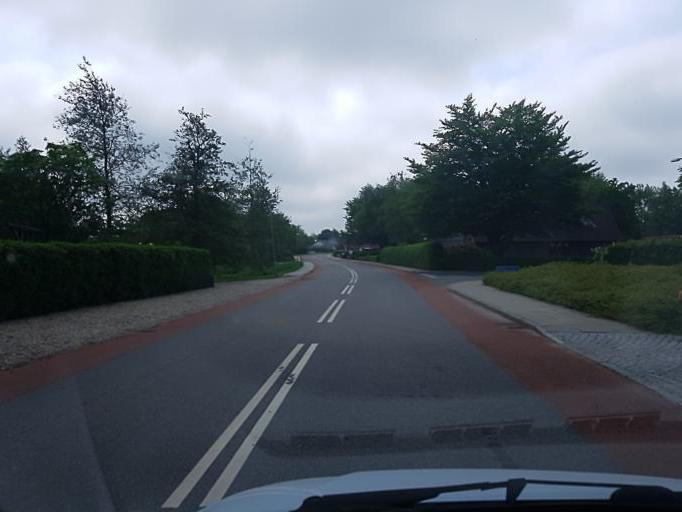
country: DK
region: South Denmark
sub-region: Esbjerg Kommune
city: Esbjerg
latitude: 55.5374
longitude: 8.4835
